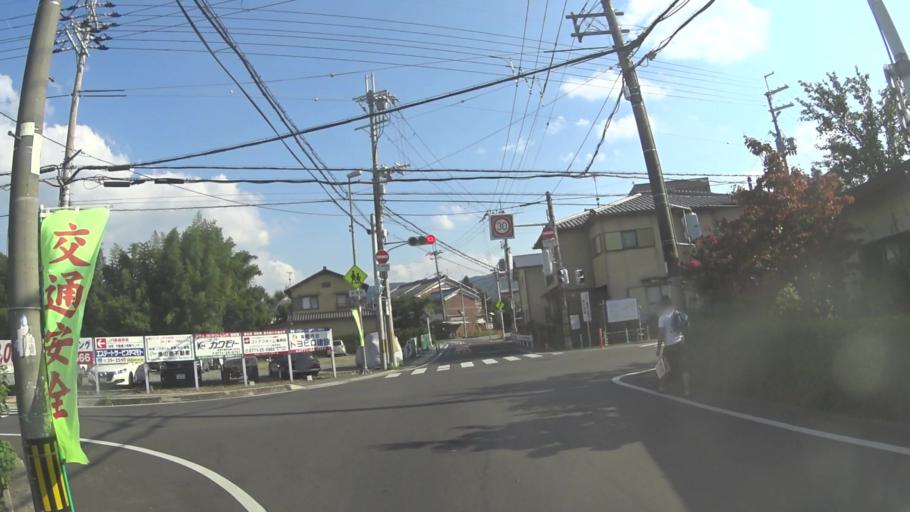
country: JP
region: Kyoto
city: Kameoka
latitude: 35.0053
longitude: 135.6026
